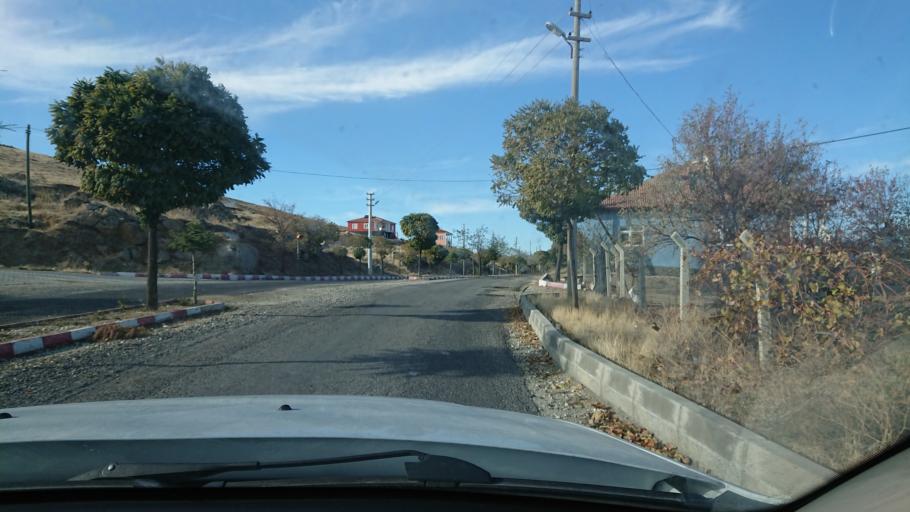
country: TR
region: Aksaray
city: Sariyahsi
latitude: 38.9641
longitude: 33.8760
